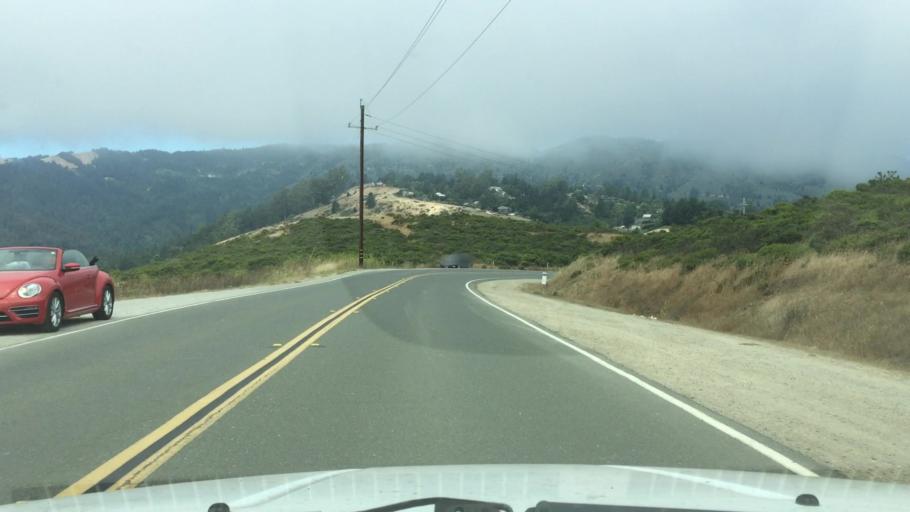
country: US
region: California
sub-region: Marin County
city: Tamalpais Valley
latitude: 37.8900
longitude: -122.5556
